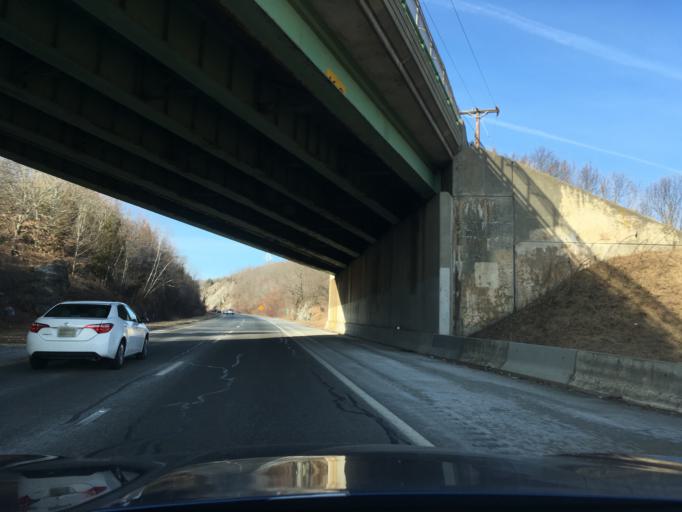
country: US
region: Rhode Island
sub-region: Providence County
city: Cranston
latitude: 41.7666
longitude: -71.4818
